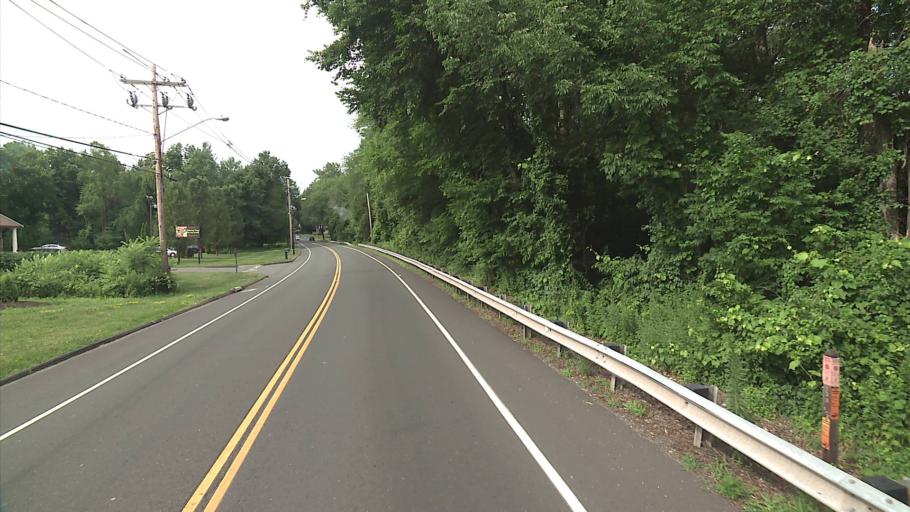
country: US
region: Connecticut
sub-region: New Haven County
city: Wallingford
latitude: 41.4797
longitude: -72.8279
